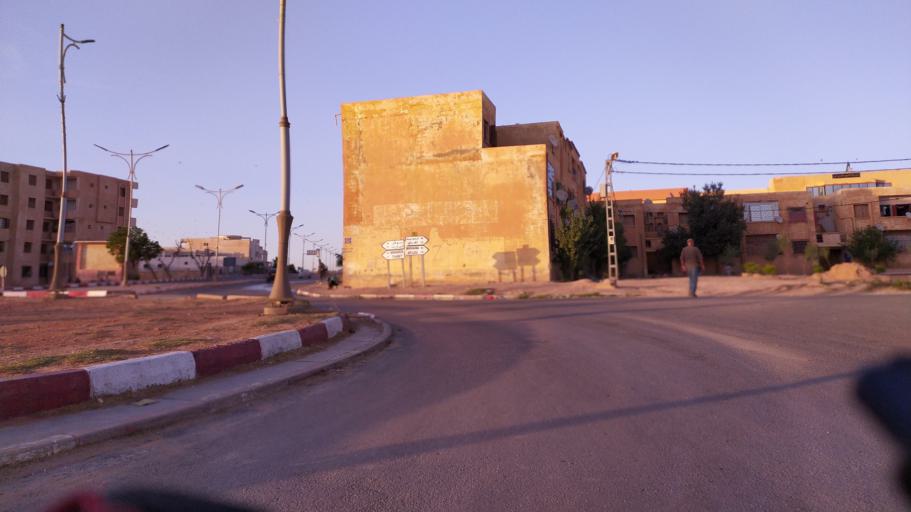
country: DZ
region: Tiaret
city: Frenda
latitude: 34.8970
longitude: 1.2481
